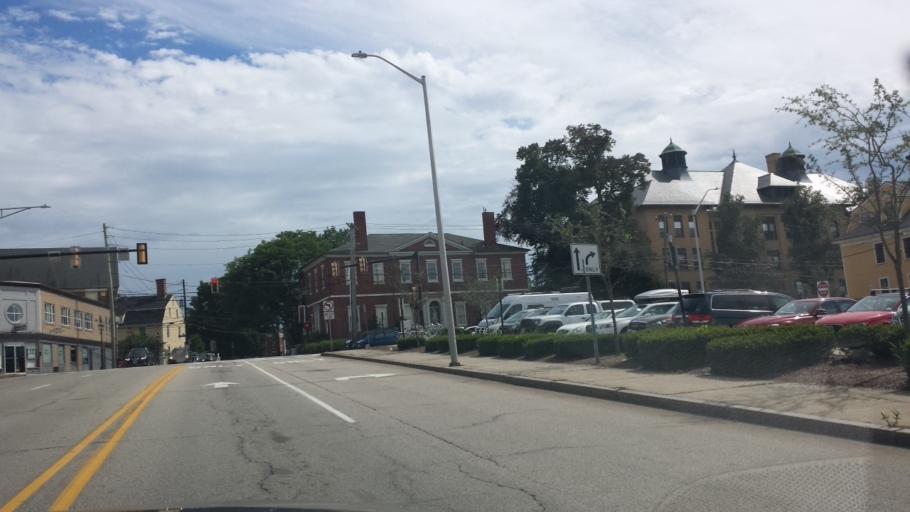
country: US
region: New Hampshire
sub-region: Rockingham County
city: Portsmouth
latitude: 43.0763
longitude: -70.7610
